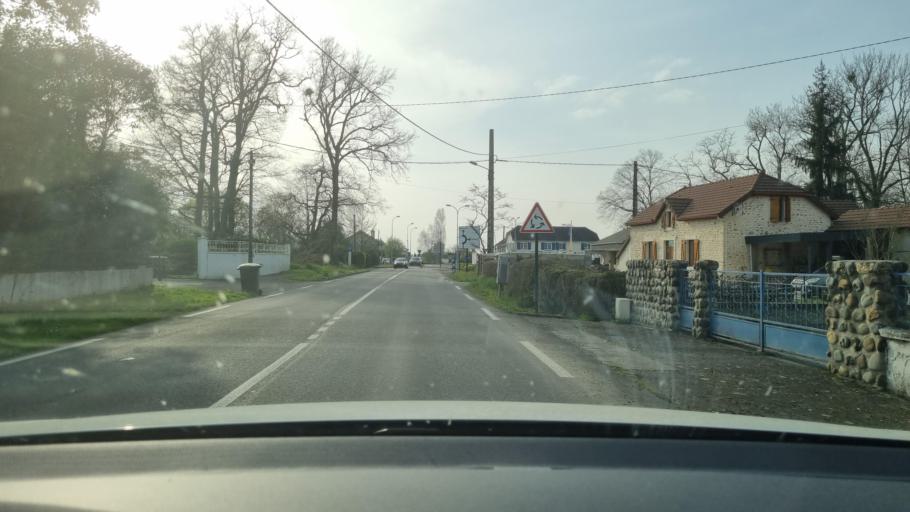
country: FR
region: Aquitaine
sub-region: Departement des Pyrenees-Atlantiques
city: Morlaas
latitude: 43.3589
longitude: -0.2427
